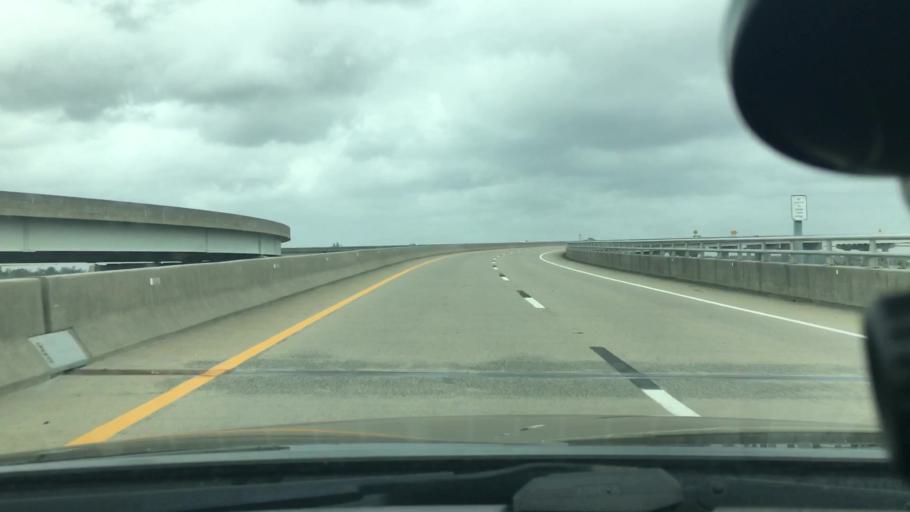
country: US
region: North Carolina
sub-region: Craven County
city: James City
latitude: 35.0928
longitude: -77.0348
